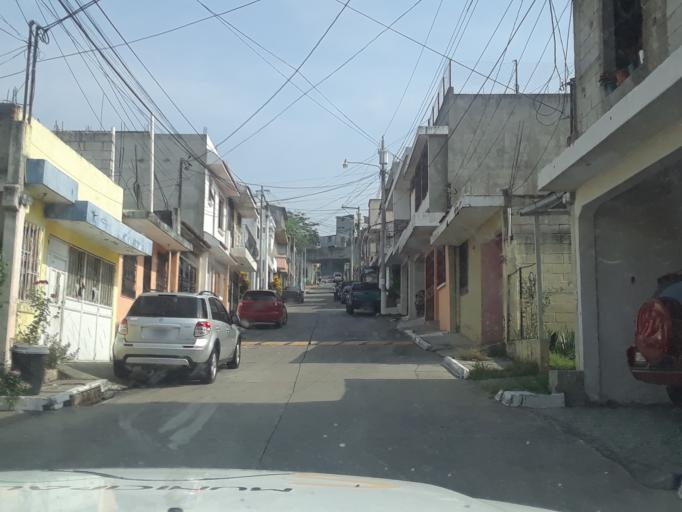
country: GT
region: Guatemala
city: Petapa
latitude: 14.5331
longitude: -90.5531
